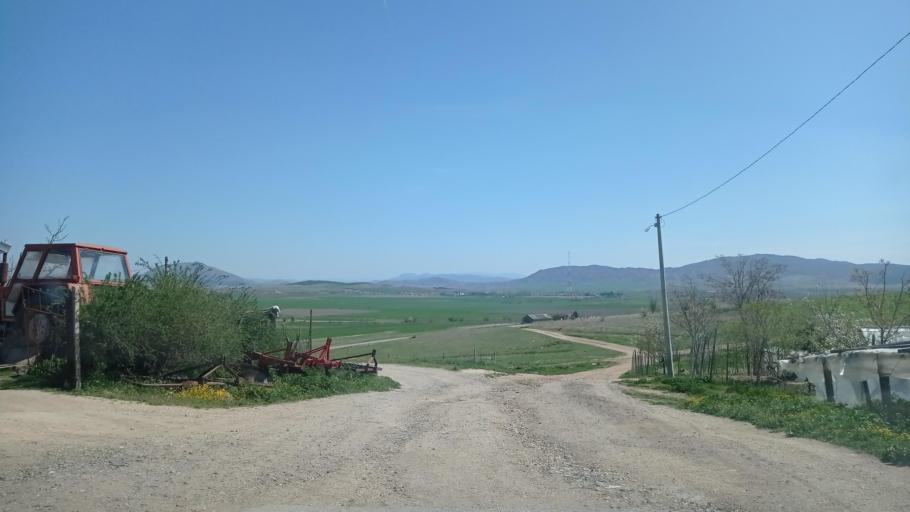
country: MK
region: Lozovo
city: Lozovo
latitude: 41.8026
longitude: 21.8680
